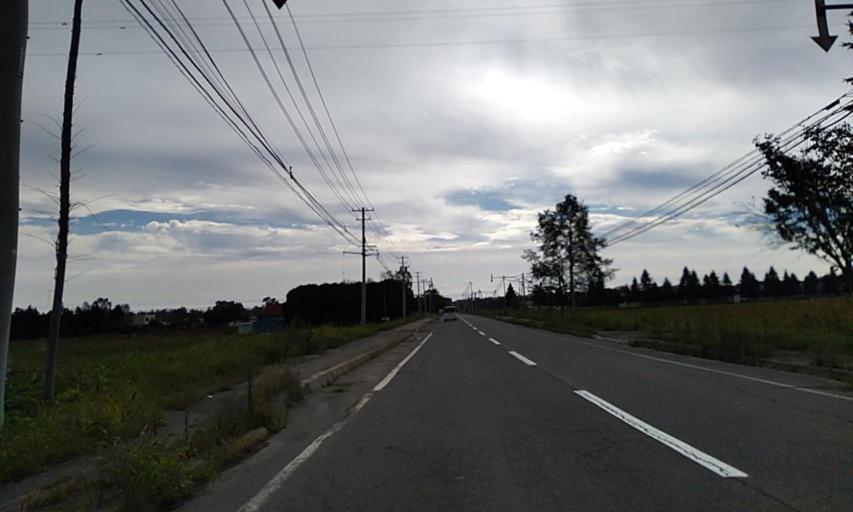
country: JP
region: Hokkaido
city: Obihiro
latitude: 42.8454
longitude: 143.1749
